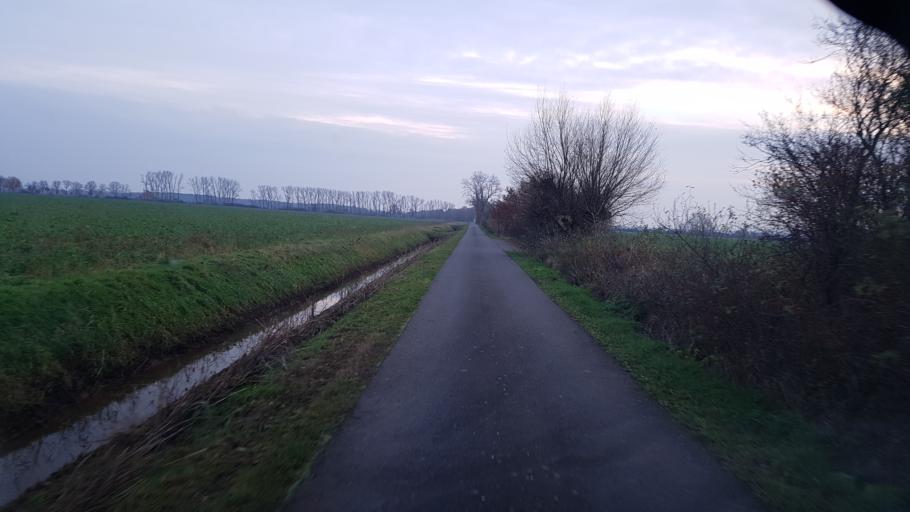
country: DE
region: Brandenburg
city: Ziltendorf
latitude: 52.2320
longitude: 14.6644
